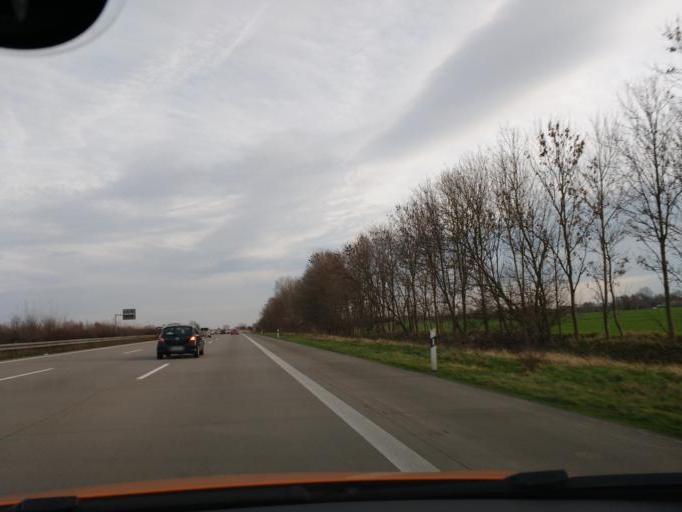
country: DE
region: Saxony-Anhalt
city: Erxleben
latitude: 52.1931
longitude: 11.2900
